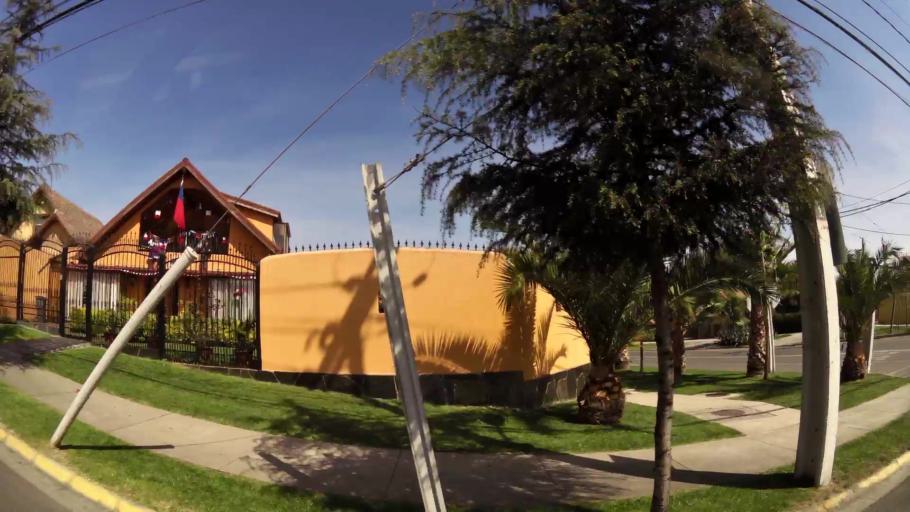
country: CL
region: Santiago Metropolitan
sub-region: Provincia de Cordillera
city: Puente Alto
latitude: -33.5358
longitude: -70.5495
